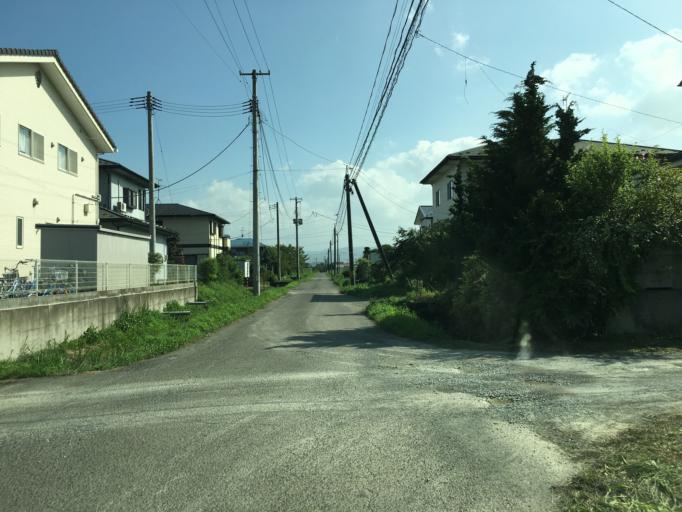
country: JP
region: Miyagi
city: Kakuda
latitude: 37.9528
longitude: 140.7801
